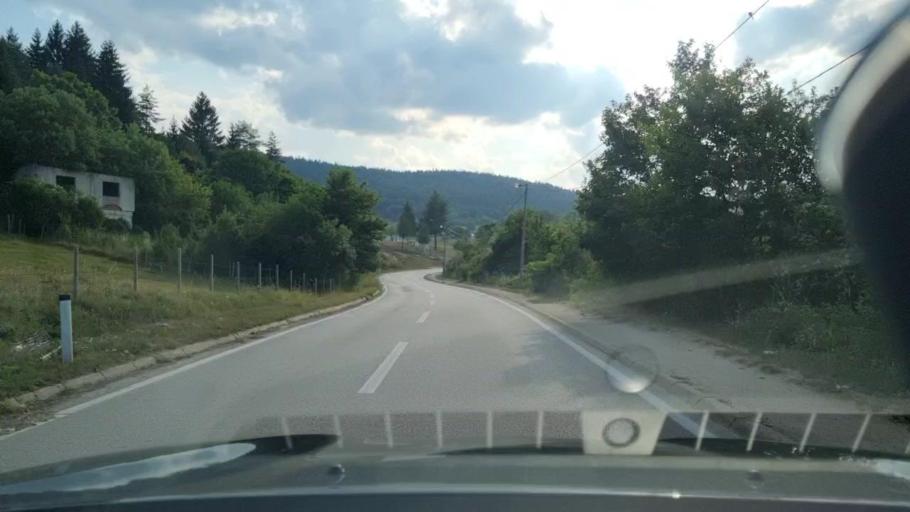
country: BA
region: Federation of Bosnia and Herzegovina
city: Glamoc
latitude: 44.0517
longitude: 16.8383
